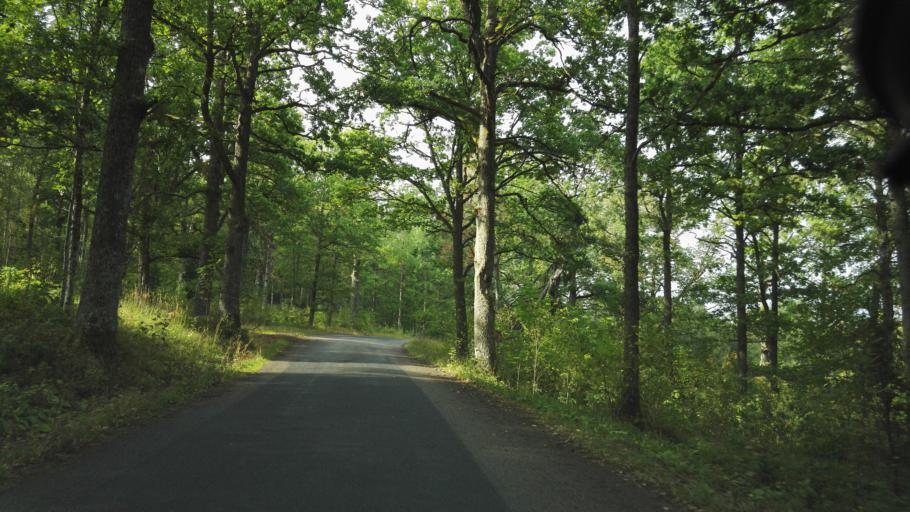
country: SE
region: Joenkoeping
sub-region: Vetlanda Kommun
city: Landsbro
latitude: 57.2402
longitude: 14.8337
